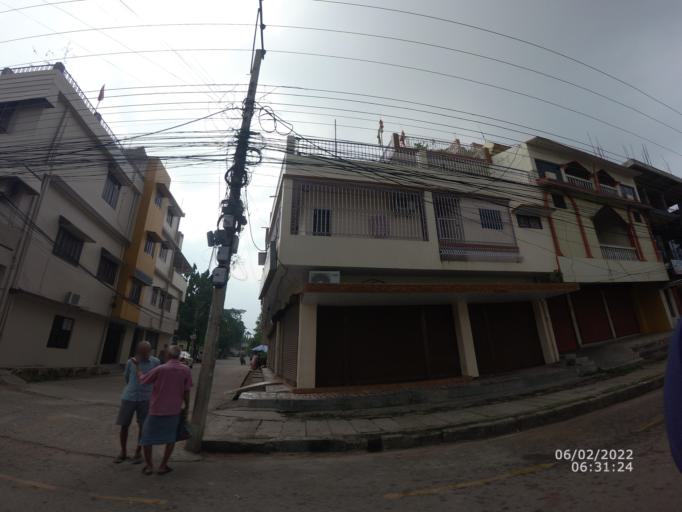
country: NP
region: Western Region
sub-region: Lumbini Zone
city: Bhairahawa
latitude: 27.5039
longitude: 83.4502
